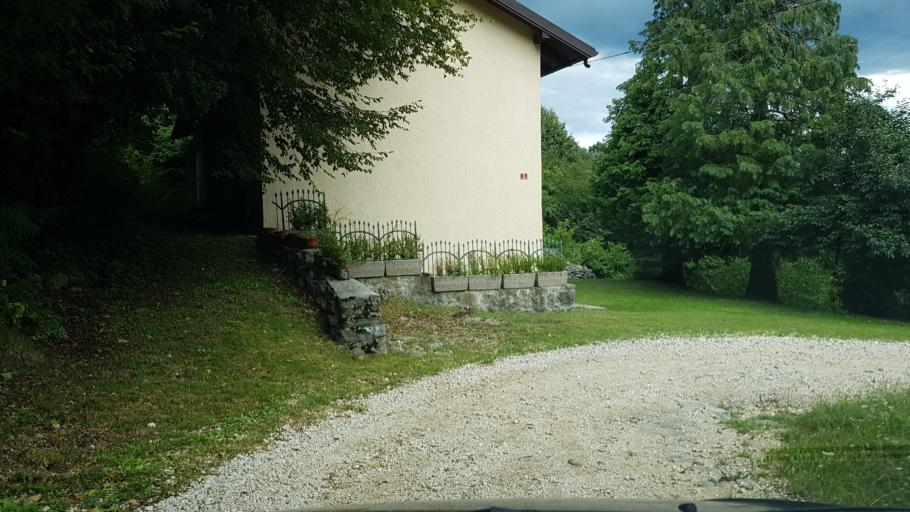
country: SI
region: Kanal
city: Deskle
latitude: 46.0619
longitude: 13.5719
